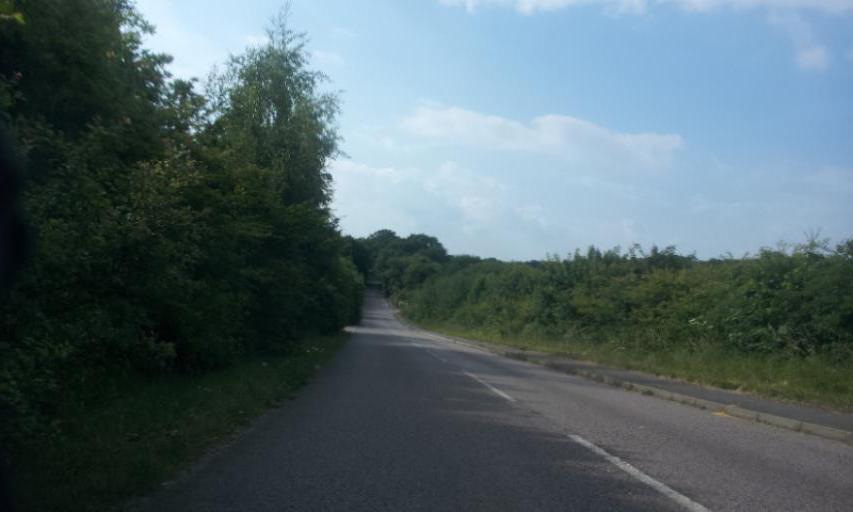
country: GB
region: England
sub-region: Kent
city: Harrietsham
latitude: 51.2326
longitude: 0.6909
